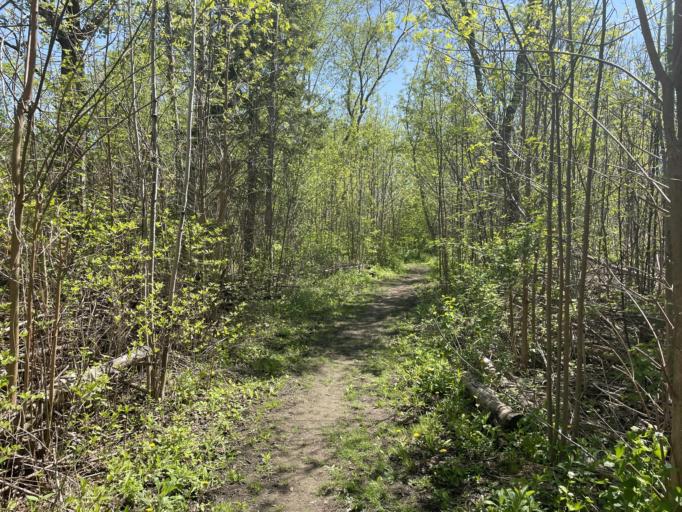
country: CA
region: Ontario
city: Oshawa
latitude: 43.8820
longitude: -78.8130
